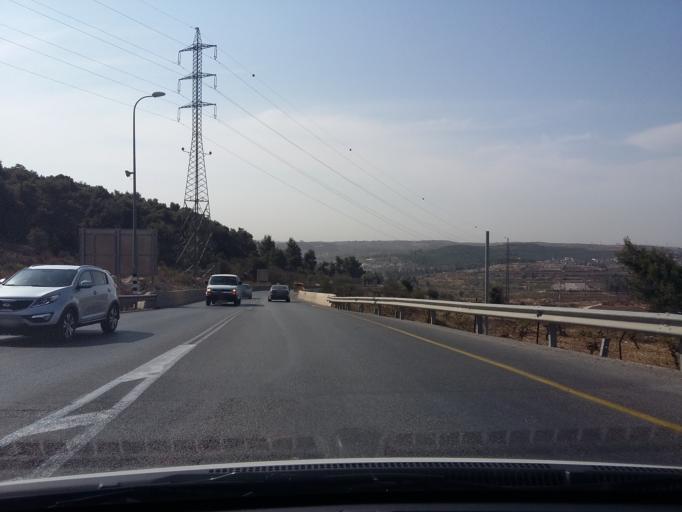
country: PS
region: West Bank
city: Shuyukh al `Arrub
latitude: 31.6439
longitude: 35.1314
